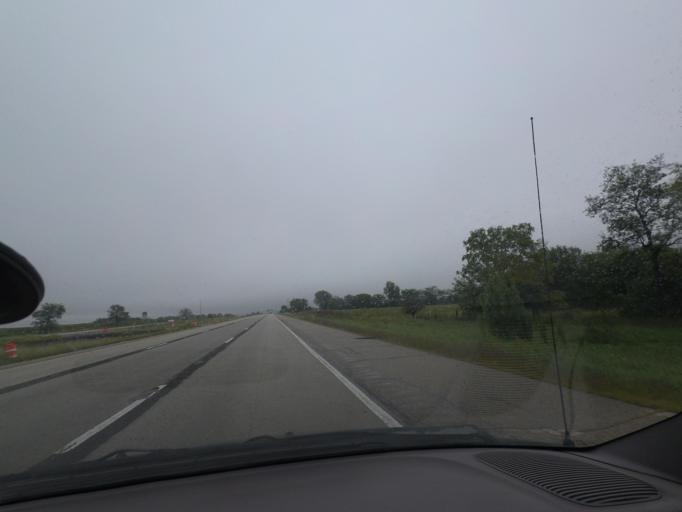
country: US
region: Illinois
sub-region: Macon County
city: Harristown
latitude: 39.8343
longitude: -89.0670
